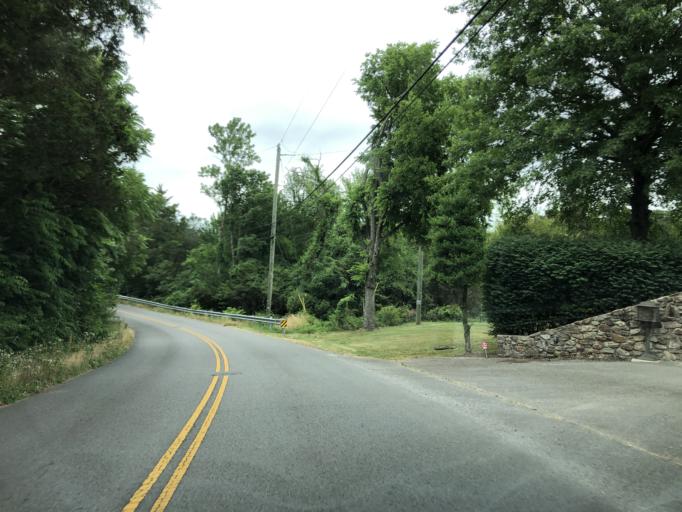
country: US
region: Tennessee
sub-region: Davidson County
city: Goodlettsville
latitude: 36.2880
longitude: -86.7307
